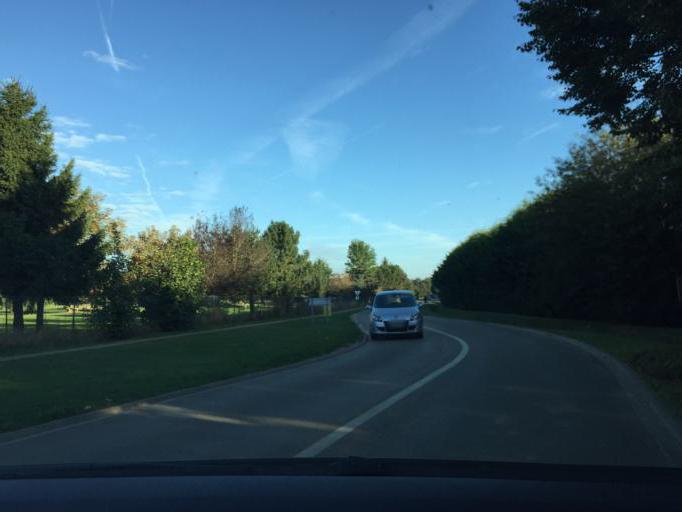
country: FR
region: Ile-de-France
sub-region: Departement de l'Essonne
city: Villiers-le-Bacle
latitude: 48.7178
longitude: 2.1388
